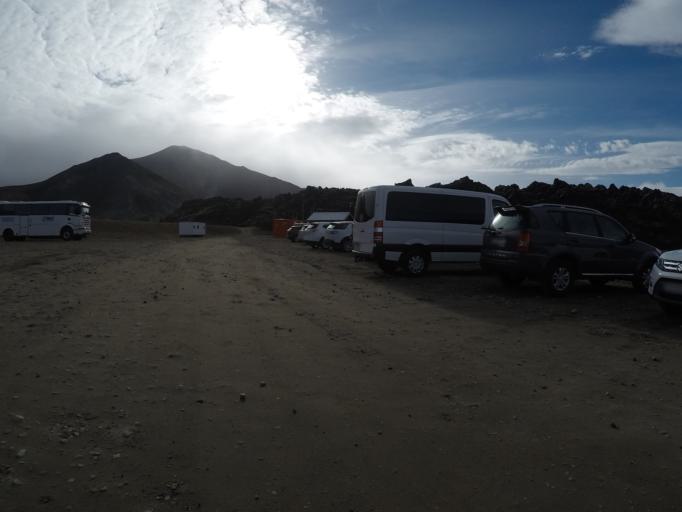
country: IS
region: South
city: Vestmannaeyjar
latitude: 63.9899
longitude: -19.0582
